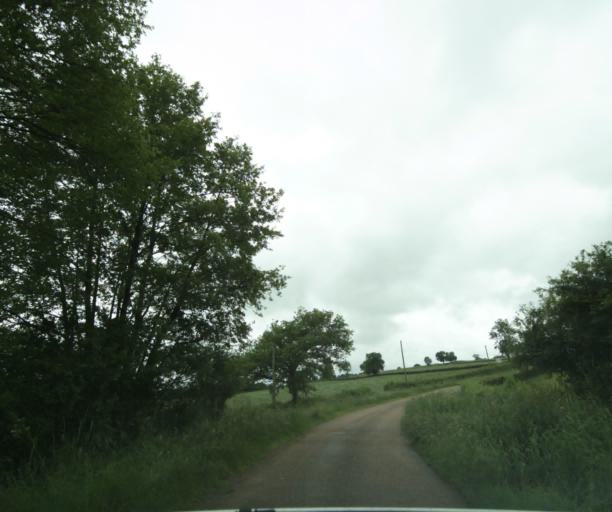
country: FR
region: Bourgogne
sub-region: Departement de Saone-et-Loire
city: Charolles
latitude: 46.4653
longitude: 4.3621
